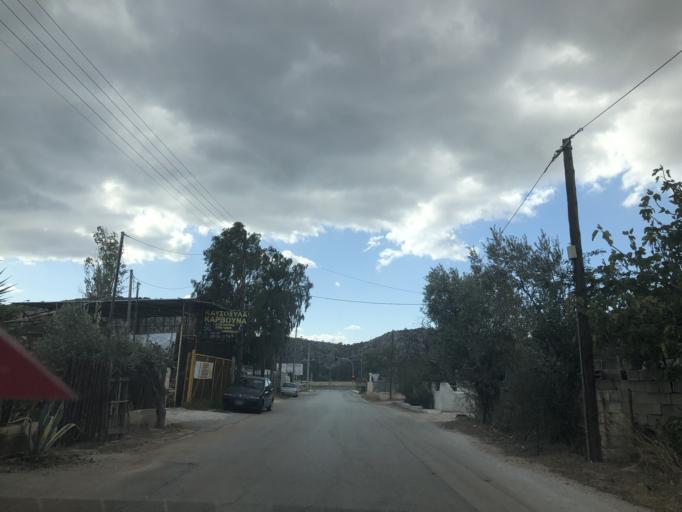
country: GR
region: Attica
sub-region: Nomarchia Anatolikis Attikis
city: Agia Marina
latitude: 37.8208
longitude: 23.8394
